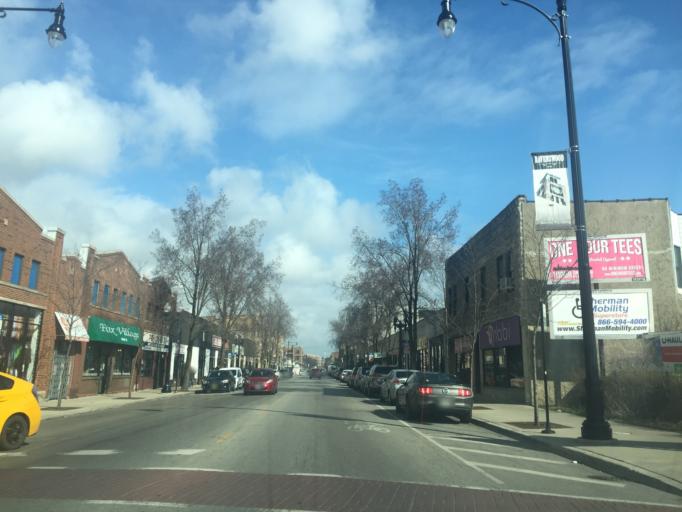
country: US
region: Illinois
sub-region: Cook County
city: Lincolnwood
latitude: 41.9634
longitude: -87.6663
